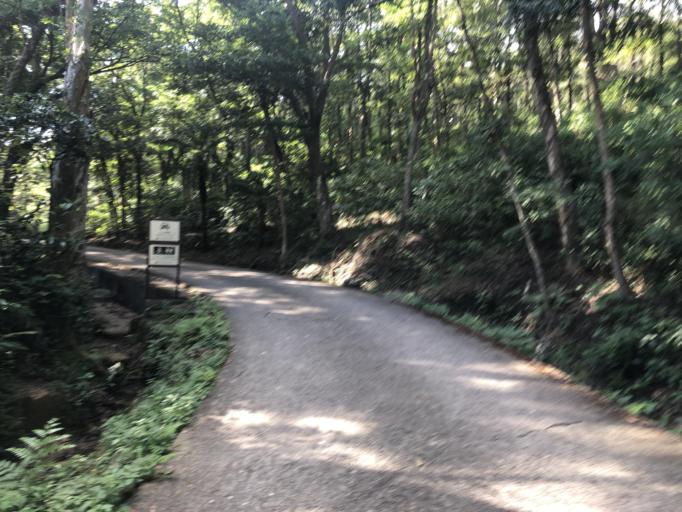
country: HK
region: Tsuen Wan
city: Tsuen Wan
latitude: 22.4074
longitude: 114.1045
